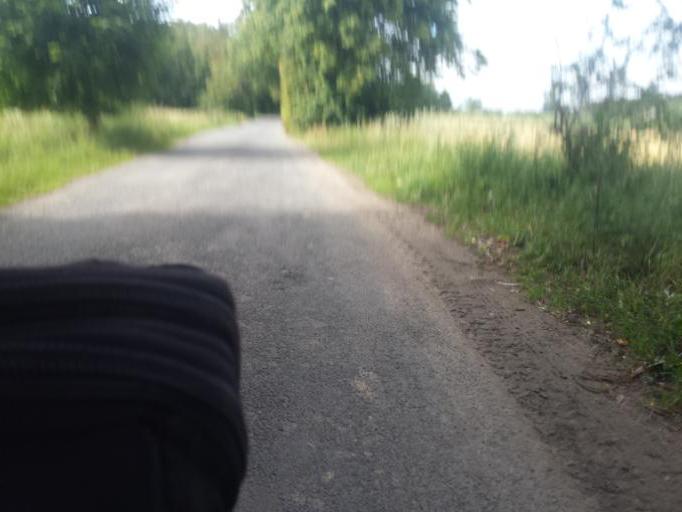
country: PL
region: Warmian-Masurian Voivodeship
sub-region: Powiat nowomiejski
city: Biskupiec
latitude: 53.5746
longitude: 19.4287
